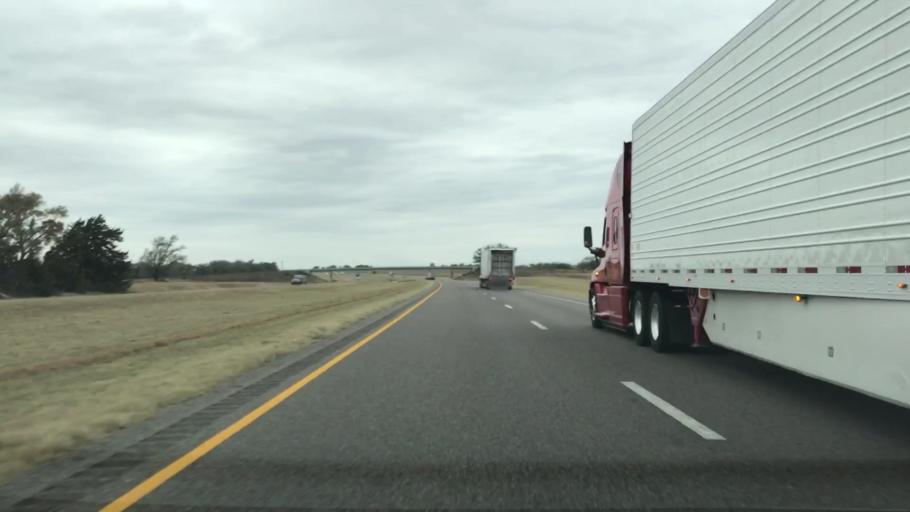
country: US
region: Oklahoma
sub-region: Beckham County
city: Erick
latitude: 35.2309
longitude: -99.9421
